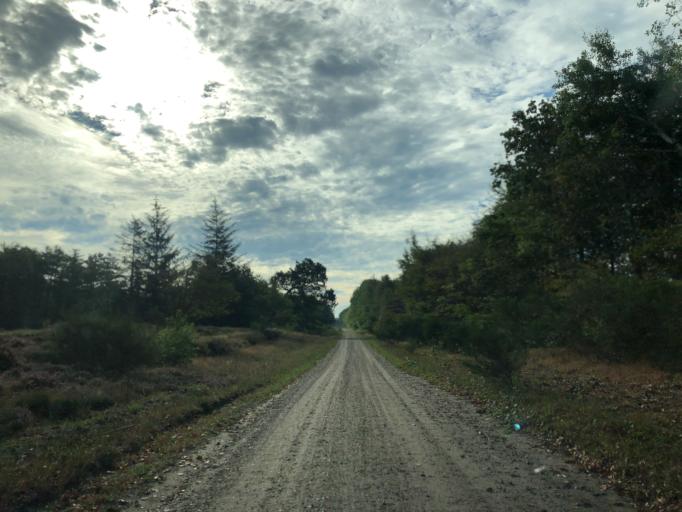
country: DK
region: Central Jutland
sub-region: Holstebro Kommune
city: Ulfborg
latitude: 56.1758
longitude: 8.3654
